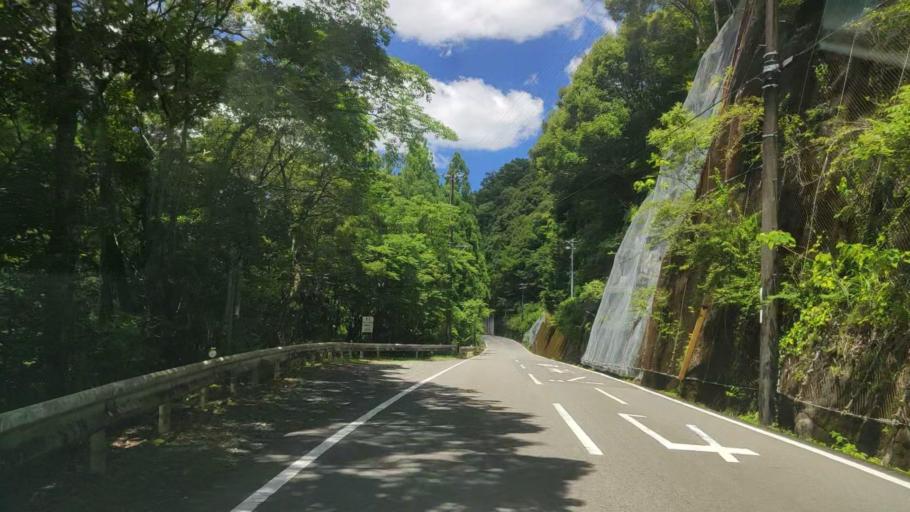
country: JP
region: Mie
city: Owase
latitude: 33.9965
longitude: 136.0127
